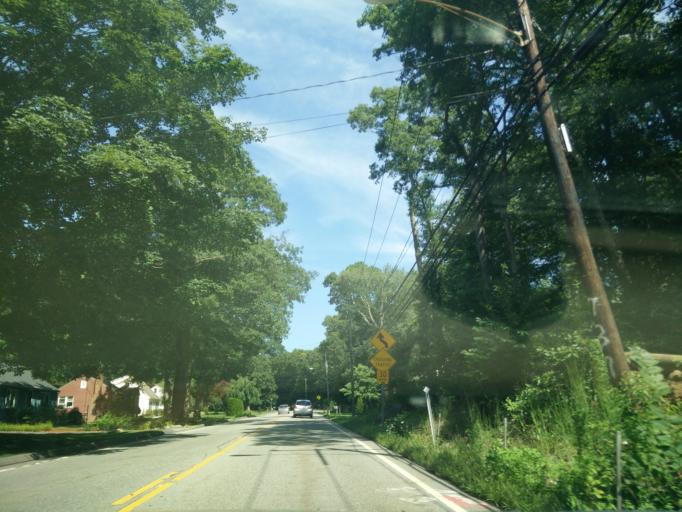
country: US
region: Connecticut
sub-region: Middlesex County
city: Clinton
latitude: 41.3030
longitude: -72.5337
